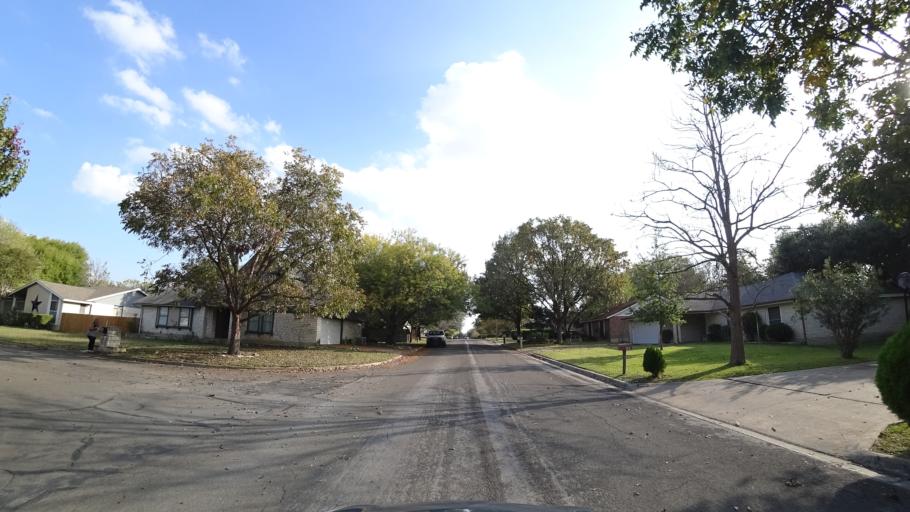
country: US
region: Texas
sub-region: Williamson County
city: Round Rock
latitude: 30.4935
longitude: -97.6717
